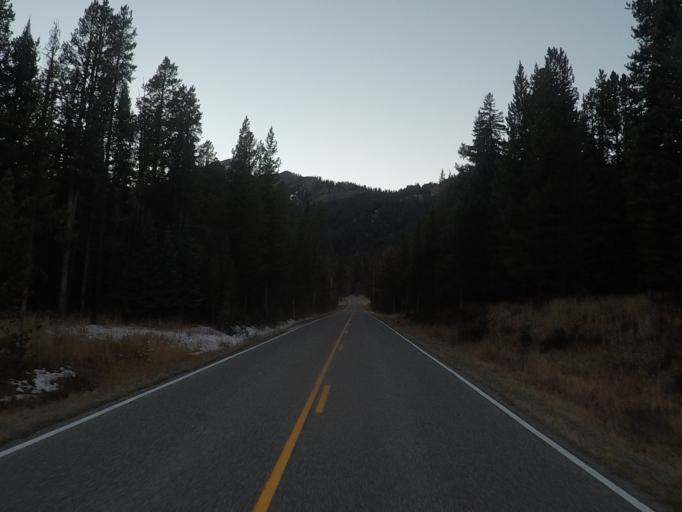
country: US
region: Montana
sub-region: Stillwater County
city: Absarokee
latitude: 45.0047
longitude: -110.0360
